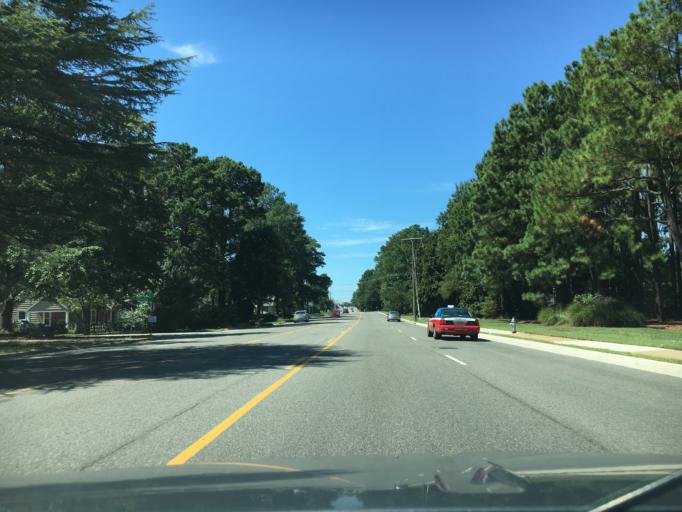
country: US
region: Virginia
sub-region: Henrico County
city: Tuckahoe
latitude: 37.6003
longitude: -77.5489
